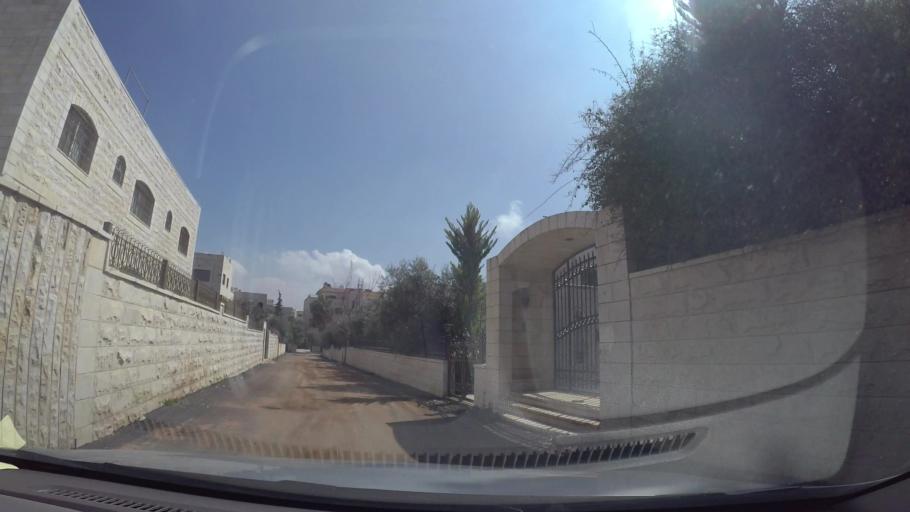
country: JO
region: Amman
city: Al Bunayyat ash Shamaliyah
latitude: 31.8994
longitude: 35.8880
